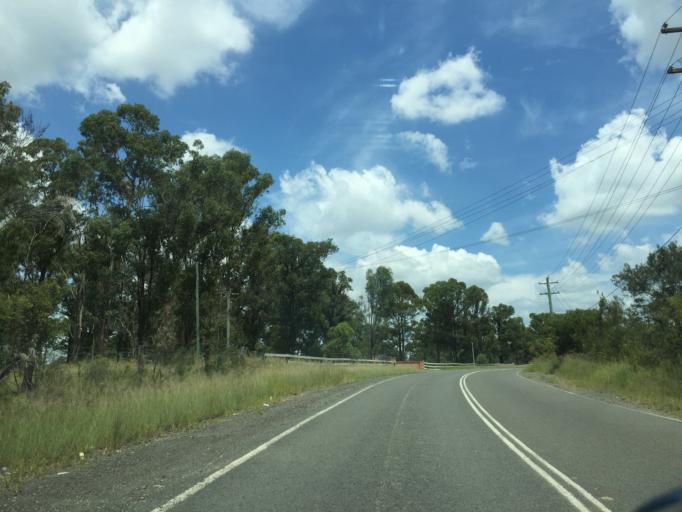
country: AU
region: New South Wales
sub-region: Blacktown
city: Hassall Grove
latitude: -33.7211
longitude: 150.8345
